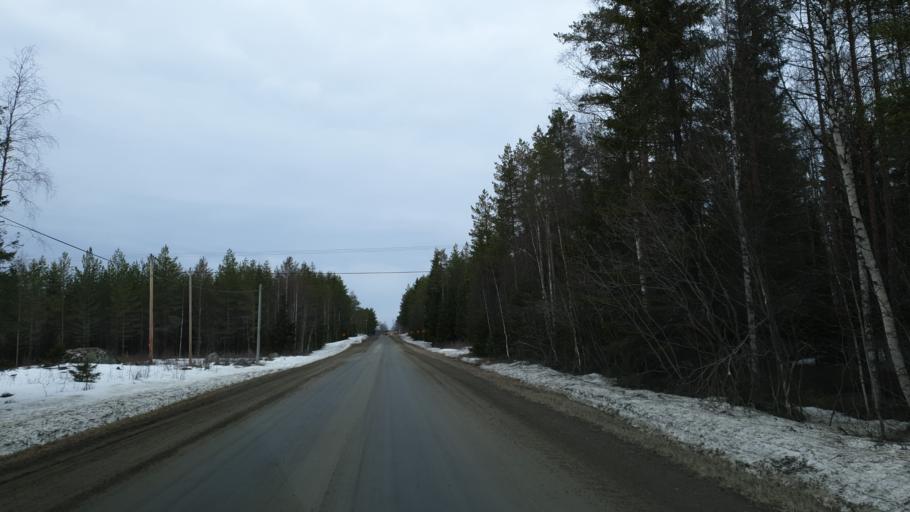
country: SE
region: Vaesterbotten
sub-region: Skelleftea Kommun
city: Burea
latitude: 64.3127
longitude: 21.1412
